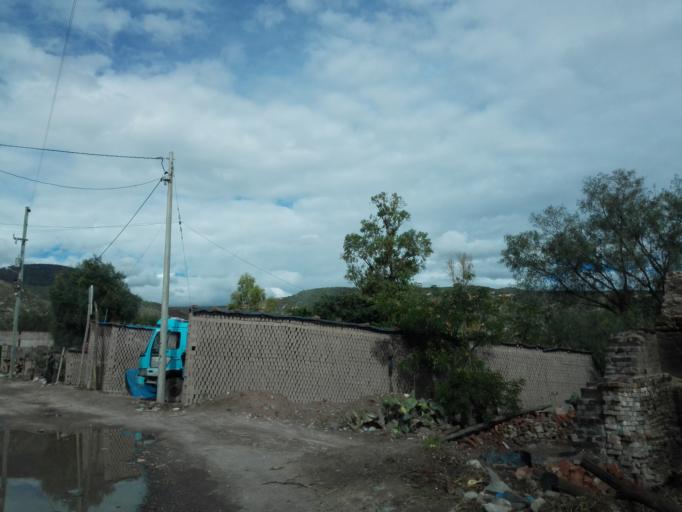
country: PE
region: Ayacucho
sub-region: Provincia de Huamanga
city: Pacaycasa
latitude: -13.0684
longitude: -74.2545
